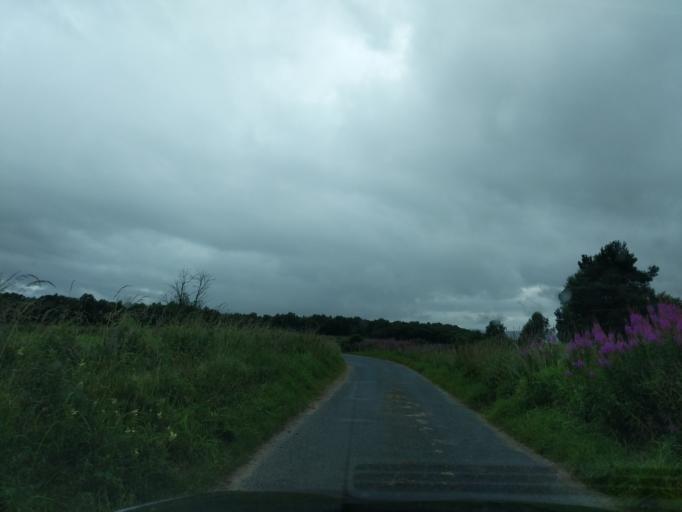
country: GB
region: Scotland
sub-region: Aberdeenshire
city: Aboyne
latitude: 57.1111
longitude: -2.8111
